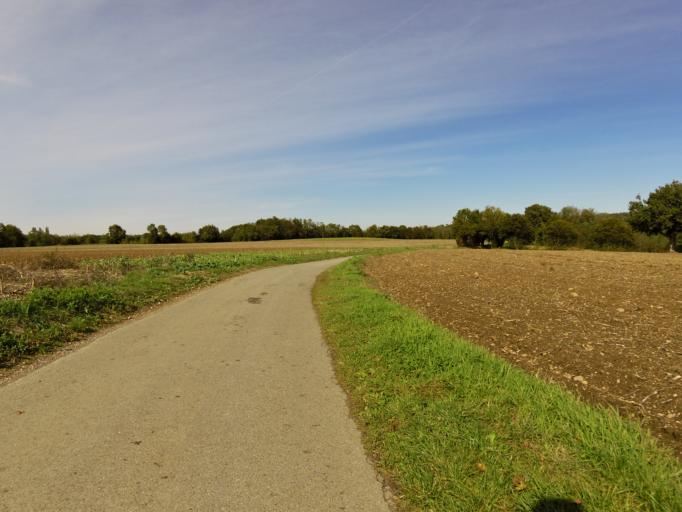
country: FR
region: Rhone-Alpes
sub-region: Departement de l'Ain
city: Perouges
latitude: 45.9194
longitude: 5.1719
